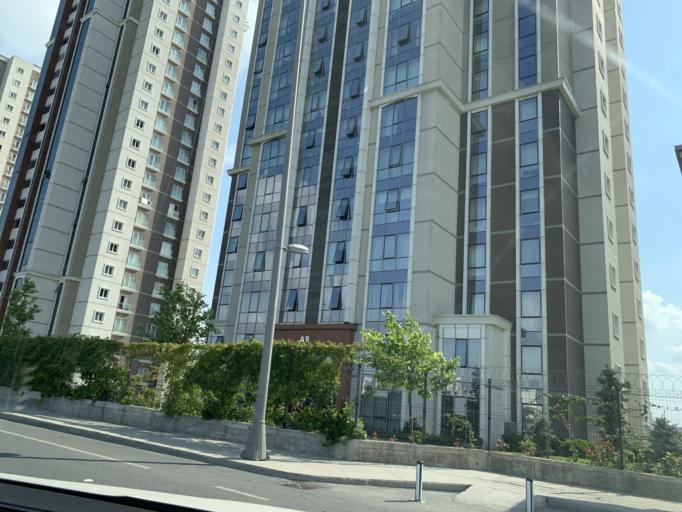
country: TR
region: Istanbul
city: Esenyurt
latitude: 41.0788
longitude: 28.6960
